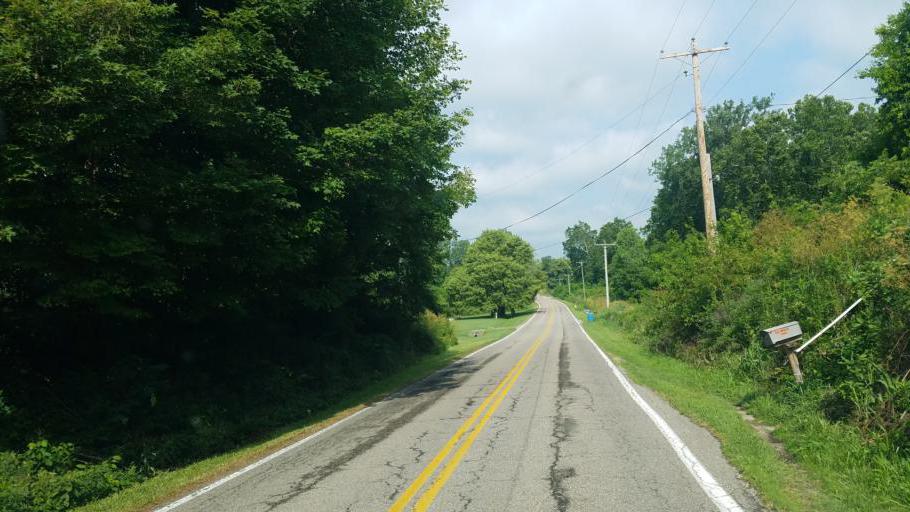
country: US
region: Ohio
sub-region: Licking County
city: Utica
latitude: 40.2522
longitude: -82.5352
